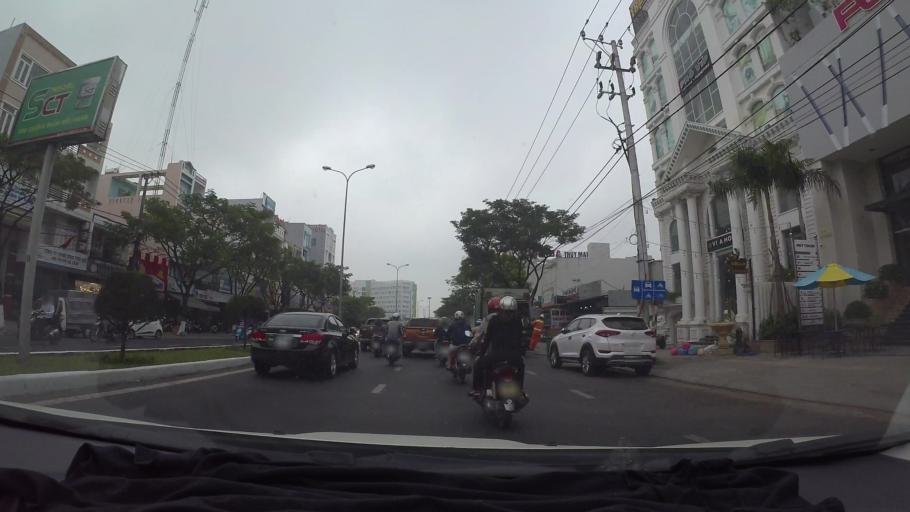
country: VN
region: Da Nang
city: Cam Le
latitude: 16.0417
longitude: 108.2103
